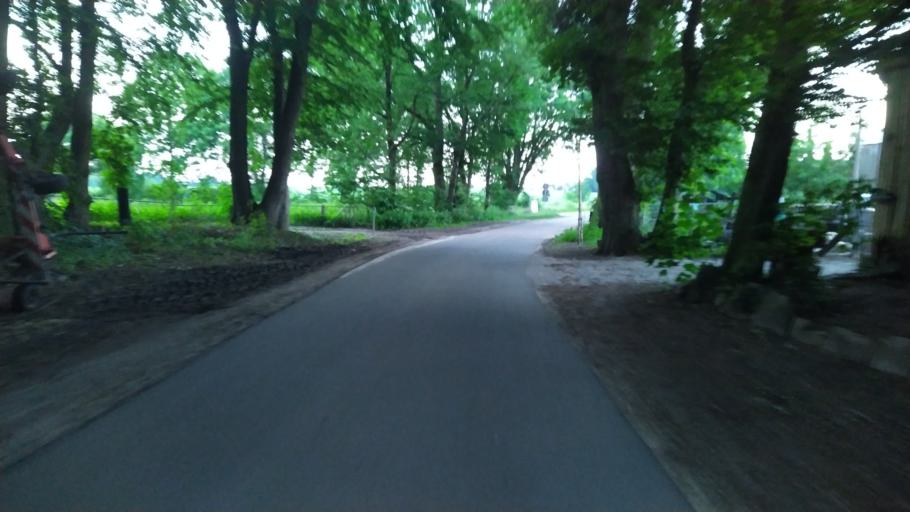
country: DE
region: Lower Saxony
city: Kutenholz
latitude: 53.5018
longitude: 9.2587
